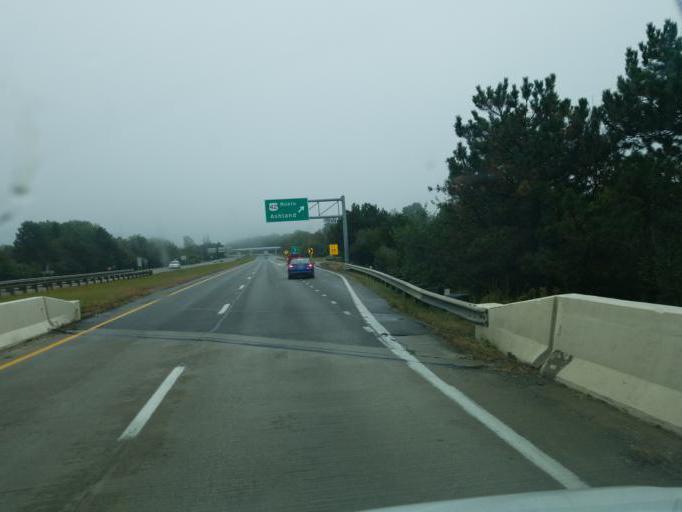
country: US
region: Ohio
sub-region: Richland County
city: Lincoln Heights
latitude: 40.7790
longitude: -82.4703
